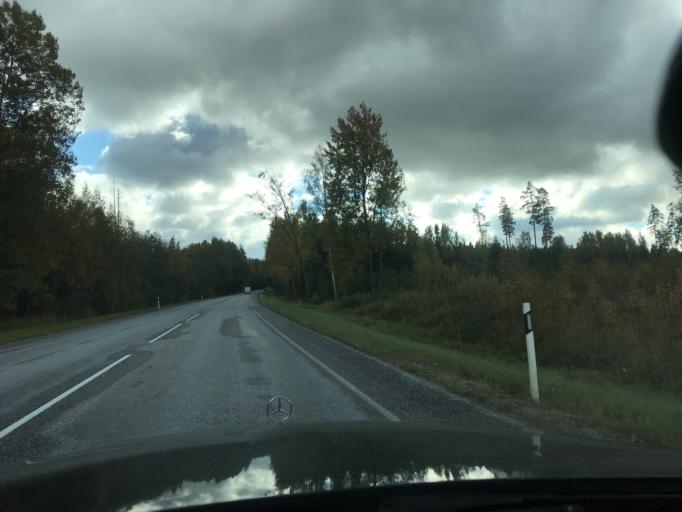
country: RU
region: Pskov
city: Pechory
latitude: 57.7254
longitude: 27.3129
